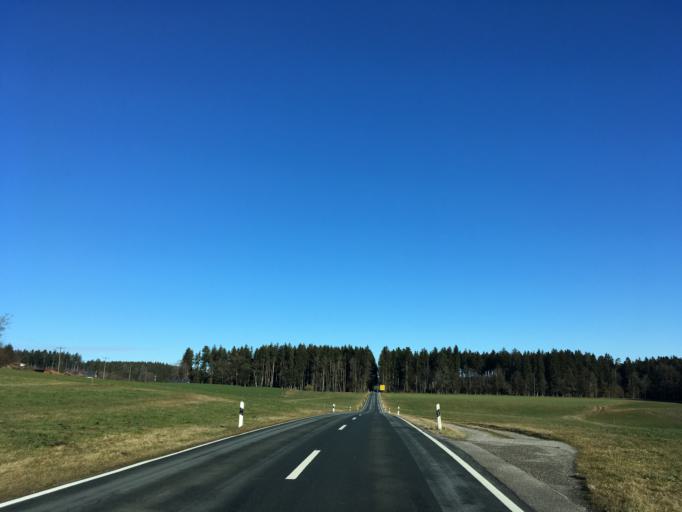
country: DE
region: Bavaria
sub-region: Upper Bavaria
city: Hoslwang
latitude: 47.9548
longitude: 12.3535
